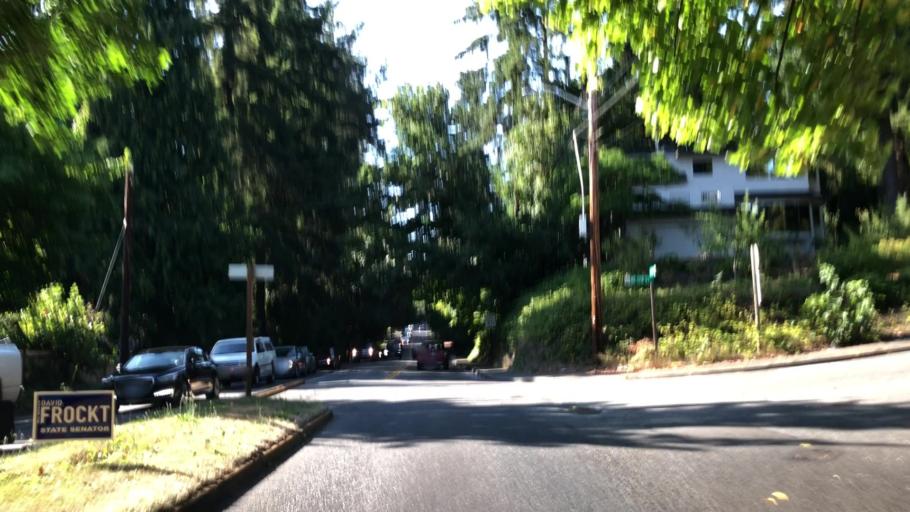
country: US
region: Washington
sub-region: King County
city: Lake Forest Park
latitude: 47.7567
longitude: -122.2807
